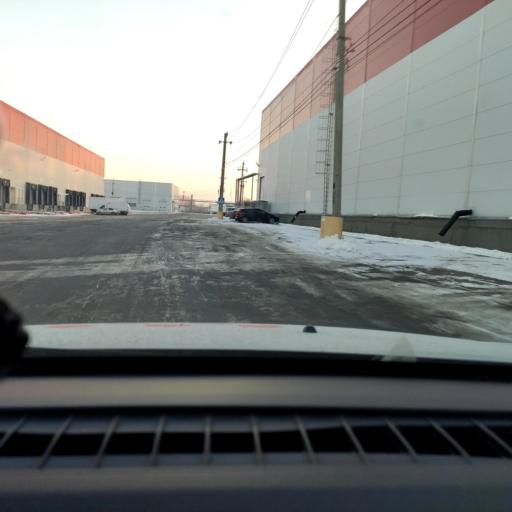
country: RU
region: Samara
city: Samara
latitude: 53.0990
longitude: 50.1346
